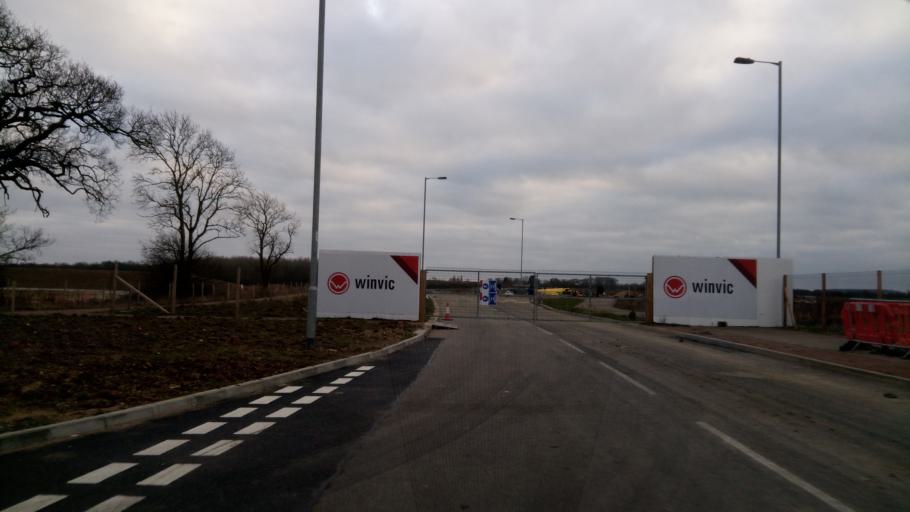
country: GB
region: England
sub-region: Cambridgeshire
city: Stilton
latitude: 52.5314
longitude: -0.3036
